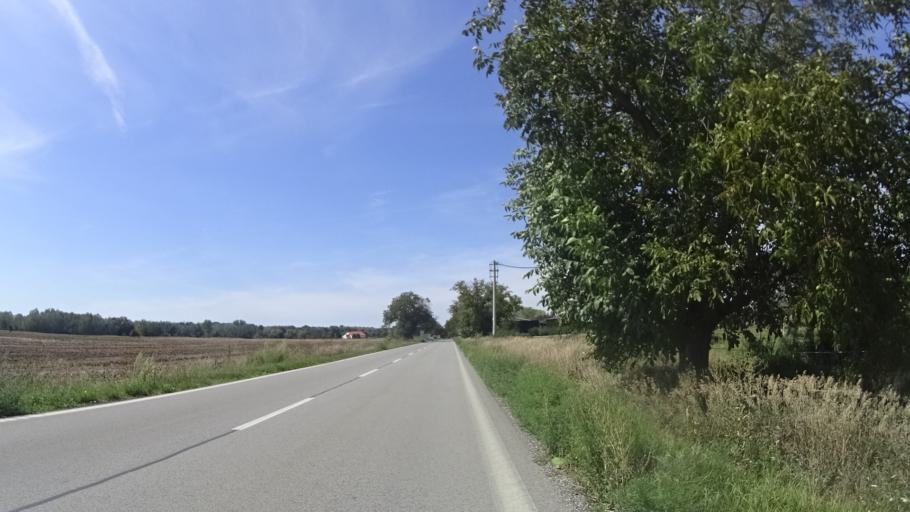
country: AT
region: Lower Austria
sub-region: Politischer Bezirk Ganserndorf
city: Marchegg
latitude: 48.3187
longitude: 16.9200
